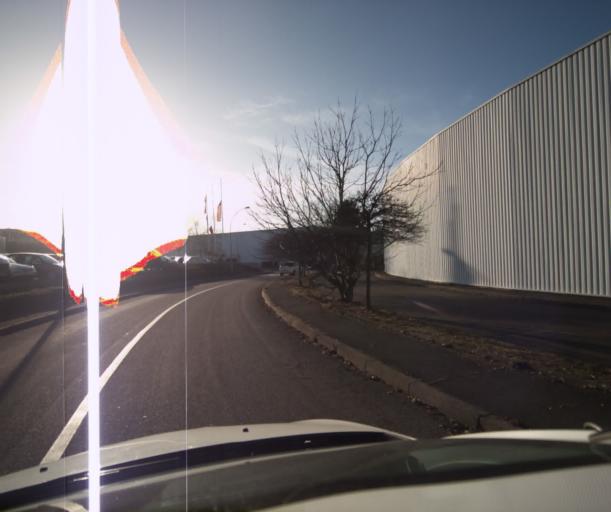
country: FR
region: Franche-Comte
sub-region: Departement du Doubs
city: Avanne-Aveney
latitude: 47.2161
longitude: 5.9525
